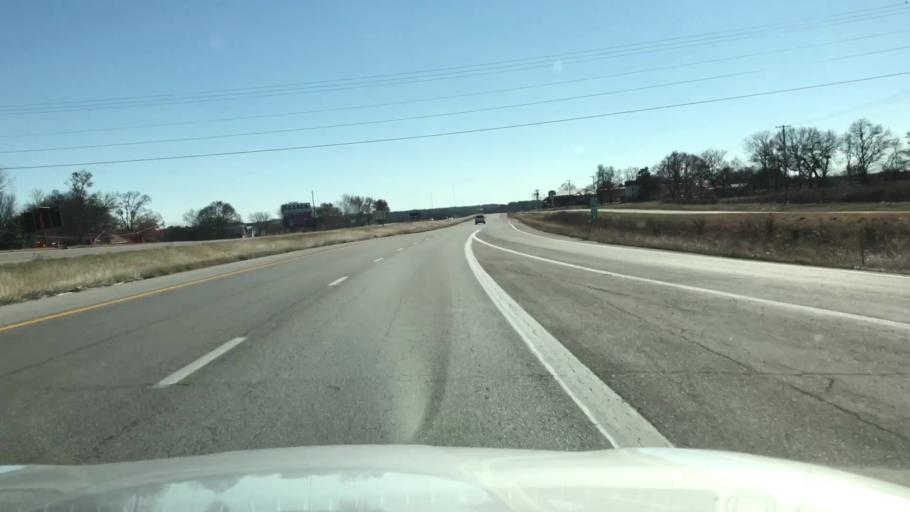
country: US
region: Missouri
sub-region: Jasper County
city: Carthage
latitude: 37.1279
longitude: -94.3110
